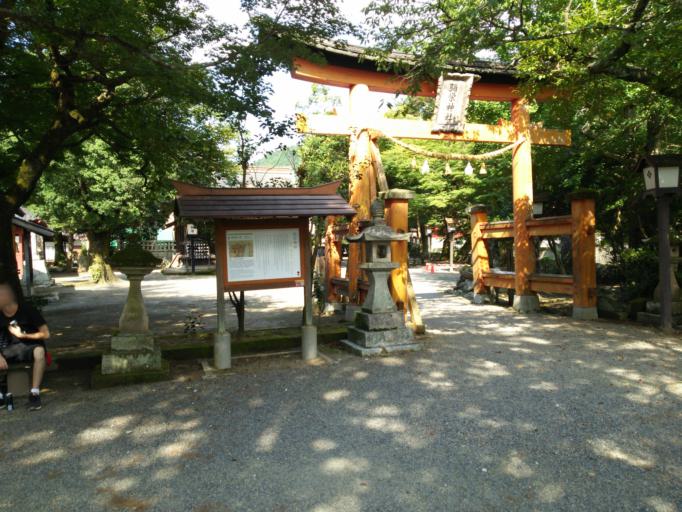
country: JP
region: Shimane
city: Masuda
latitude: 34.4657
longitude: 131.7713
